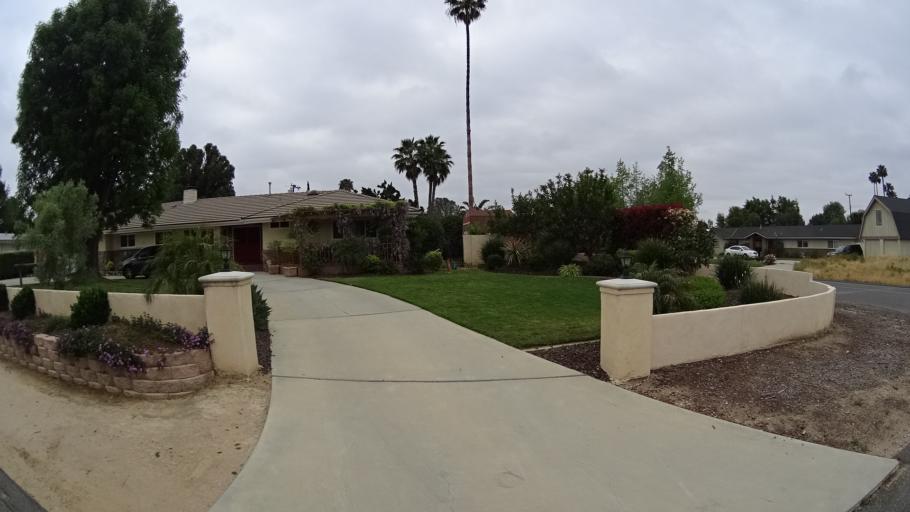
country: US
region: California
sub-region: Ventura County
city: Thousand Oaks
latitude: 34.2034
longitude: -118.8612
